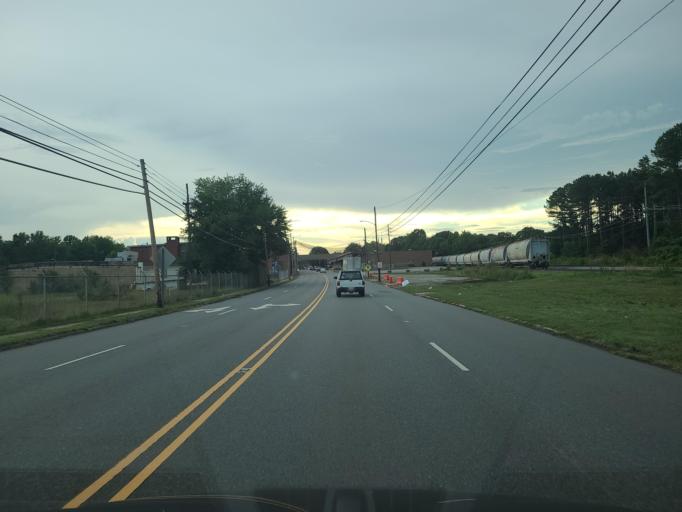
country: US
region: North Carolina
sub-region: Gaston County
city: Ranlo
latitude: 35.2788
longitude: -81.1273
